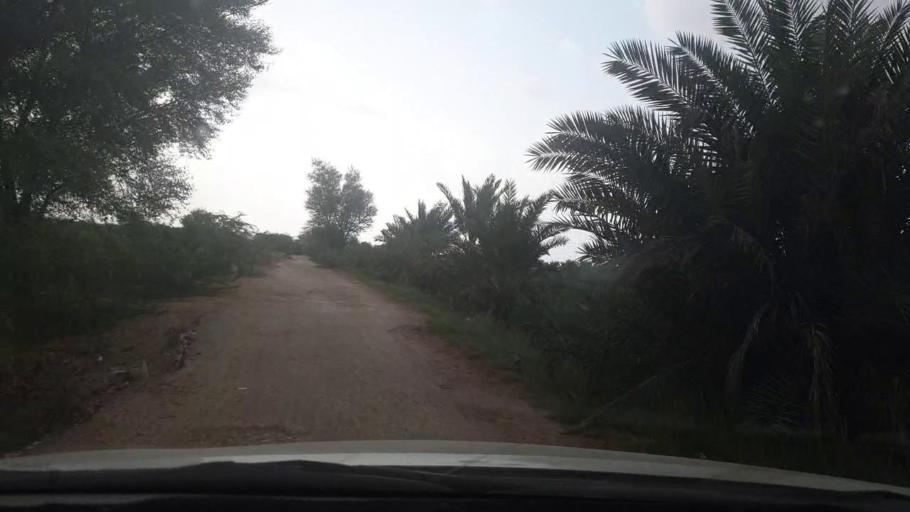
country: PK
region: Sindh
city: Khairpur
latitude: 27.4439
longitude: 68.9966
